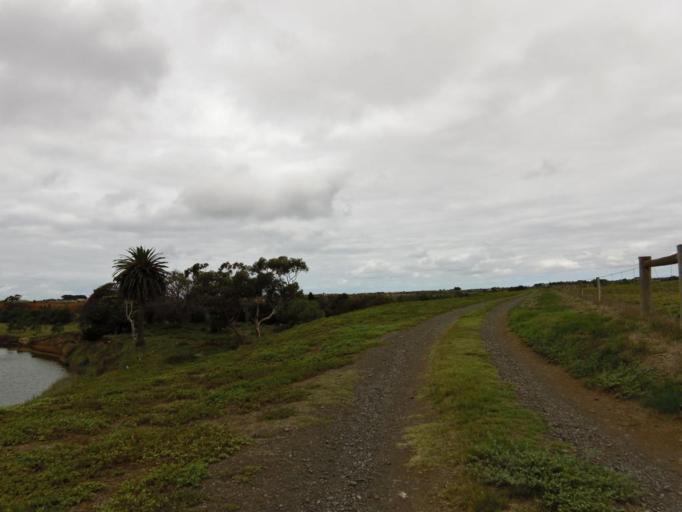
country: AU
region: Victoria
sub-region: Wyndham
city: Werribee
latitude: -37.9432
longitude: 144.6651
